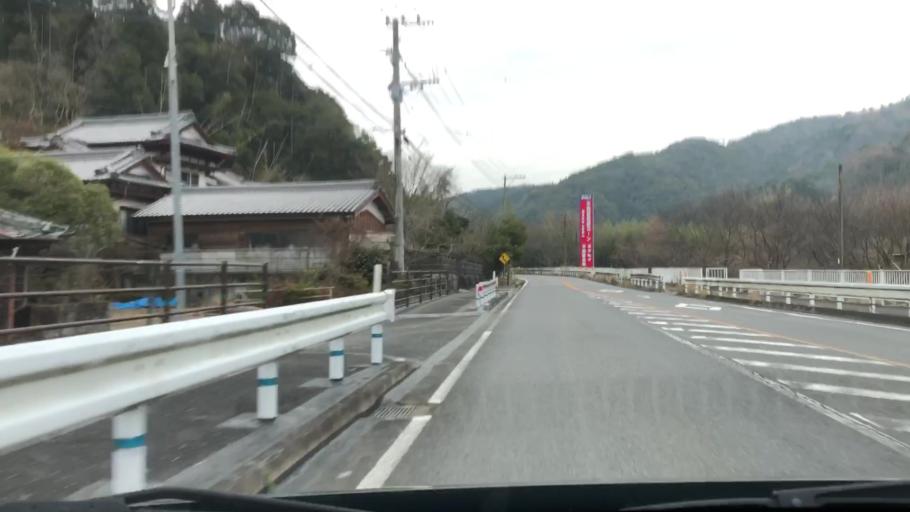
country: JP
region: Oita
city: Usuki
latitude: 33.0051
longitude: 131.7263
